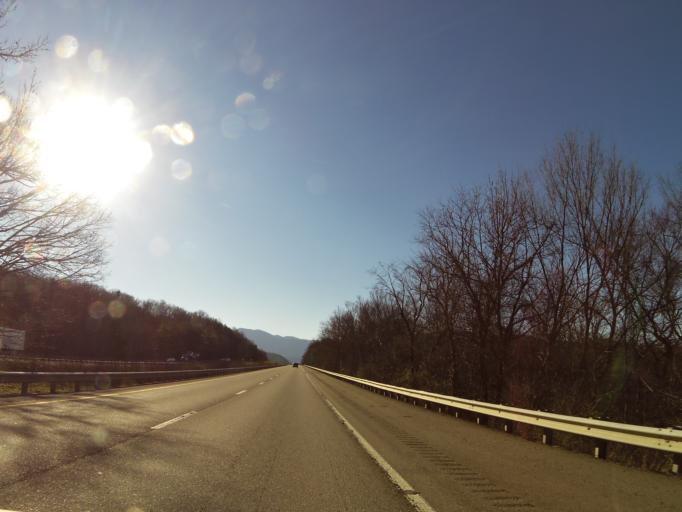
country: US
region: Tennessee
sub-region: Cocke County
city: Newport
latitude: 35.8572
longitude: -83.1842
